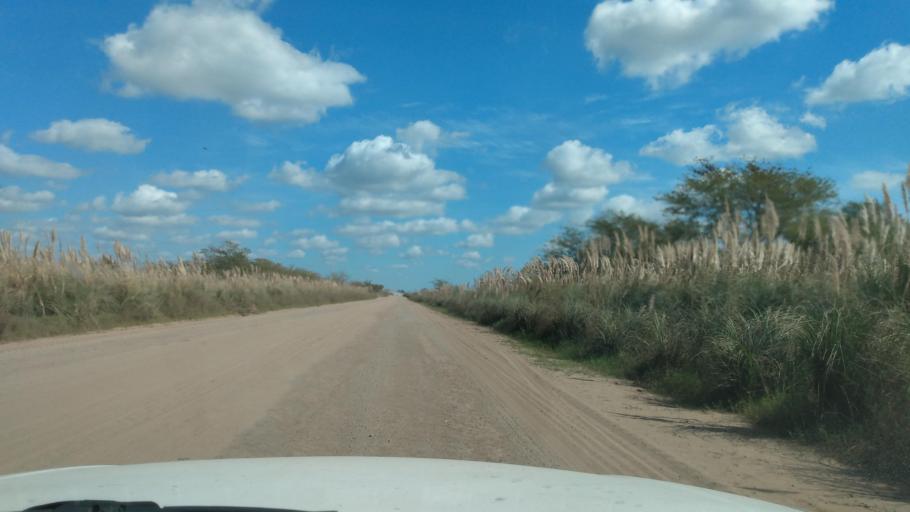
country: AR
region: Buenos Aires
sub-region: Partido de Navarro
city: Navarro
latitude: -35.0015
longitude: -59.3514
